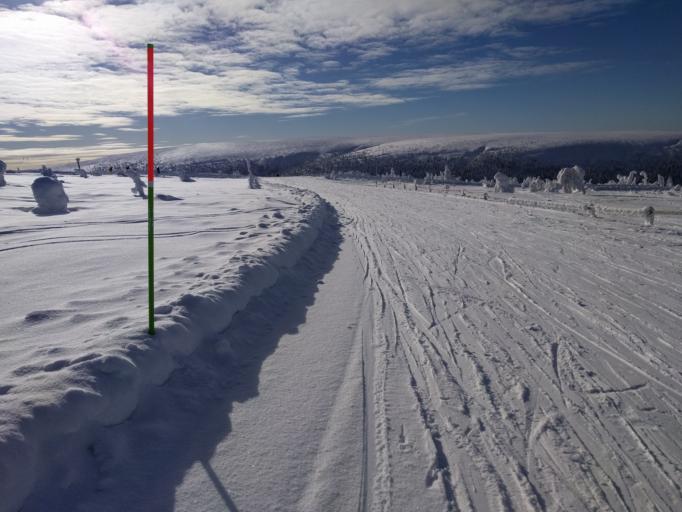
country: NO
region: Hedmark
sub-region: Trysil
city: Innbygda
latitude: 61.1746
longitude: 13.0172
